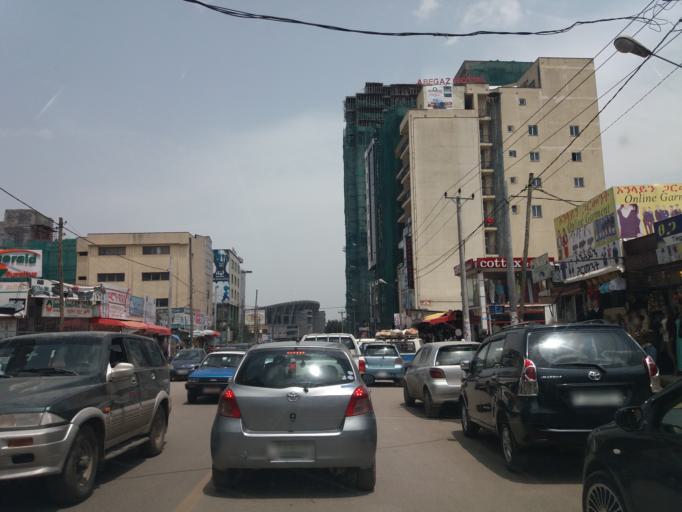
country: ET
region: Adis Abeba
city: Addis Ababa
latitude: 9.0071
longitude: 38.7890
